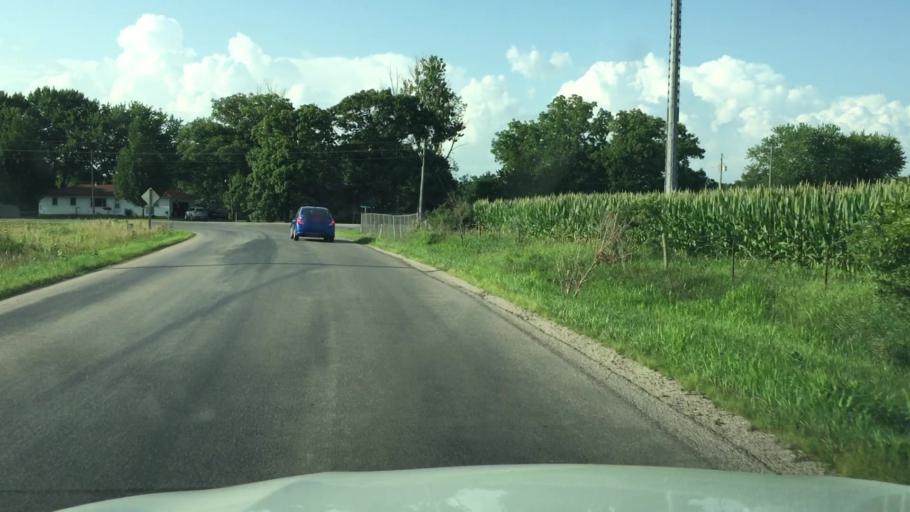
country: US
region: Iowa
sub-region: Linn County
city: Ely
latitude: 41.8265
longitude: -91.6231
